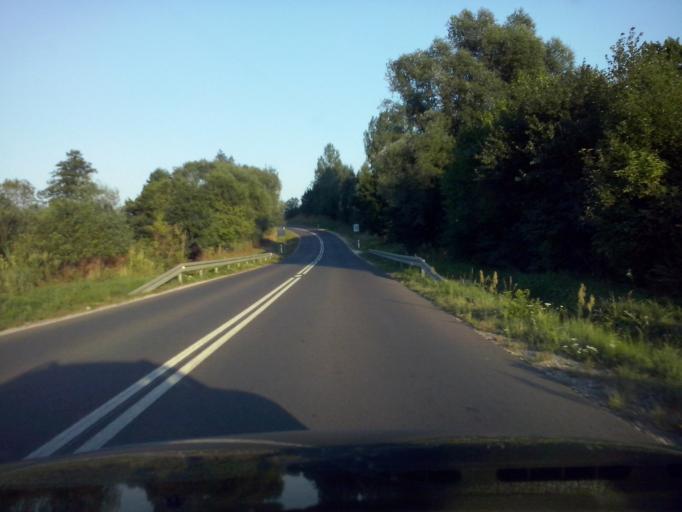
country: PL
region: Swietokrzyskie
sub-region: Powiat buski
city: Gnojno
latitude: 50.6072
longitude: 20.8175
